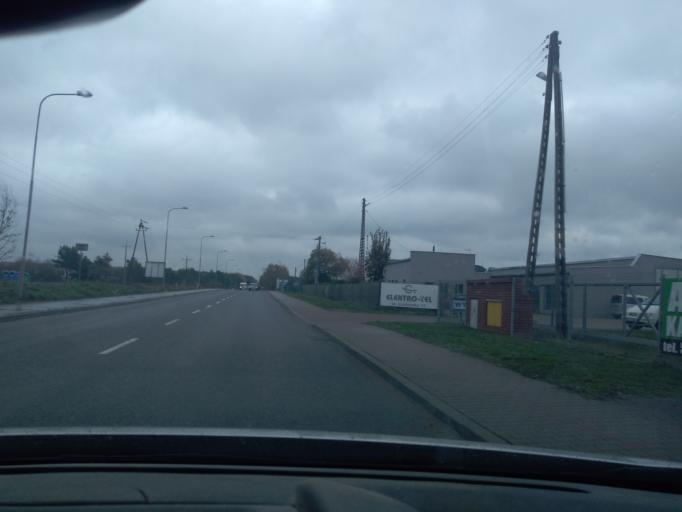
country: PL
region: Greater Poland Voivodeship
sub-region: Powiat obornicki
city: Oborniki
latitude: 52.6439
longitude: 16.8287
